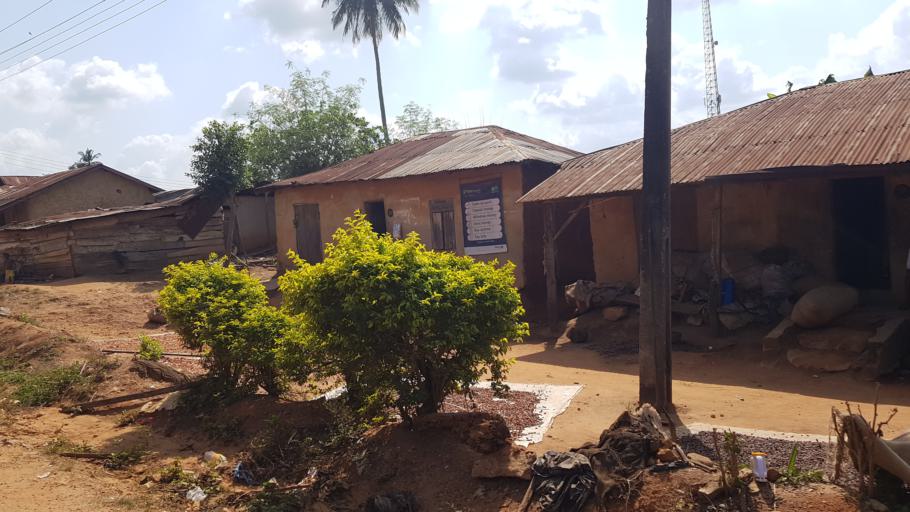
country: NG
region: Osun
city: Ifetedo
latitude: 7.0215
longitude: 4.6313
